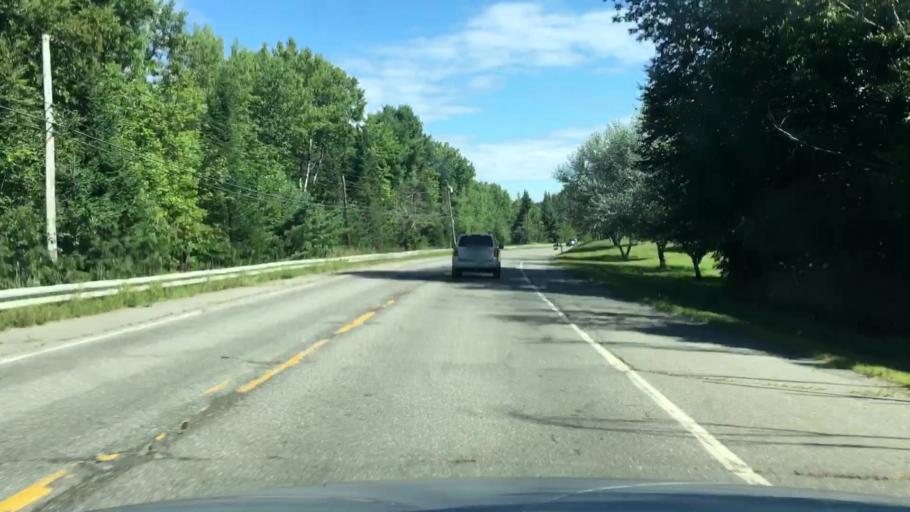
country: US
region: Maine
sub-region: Penobscot County
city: Dexter
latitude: 45.0464
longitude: -69.2712
